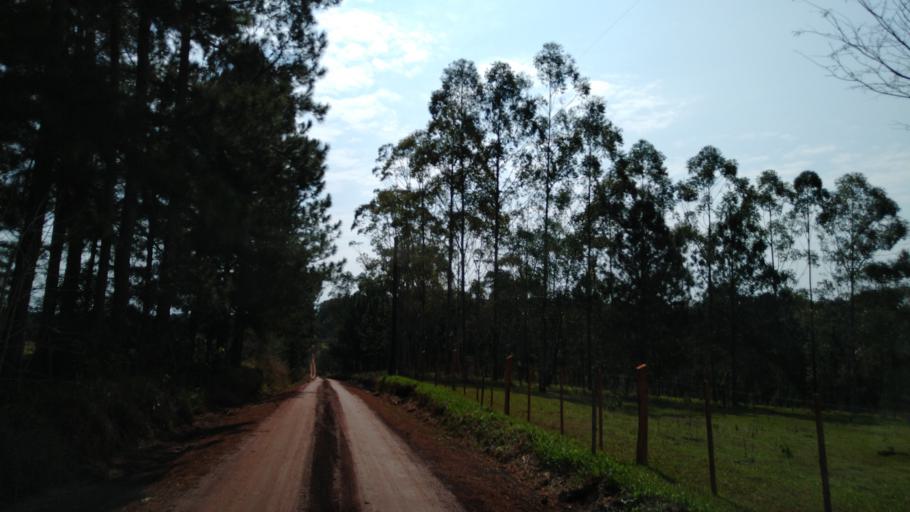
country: AR
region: Misiones
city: Capiovi
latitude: -26.9489
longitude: -55.0441
